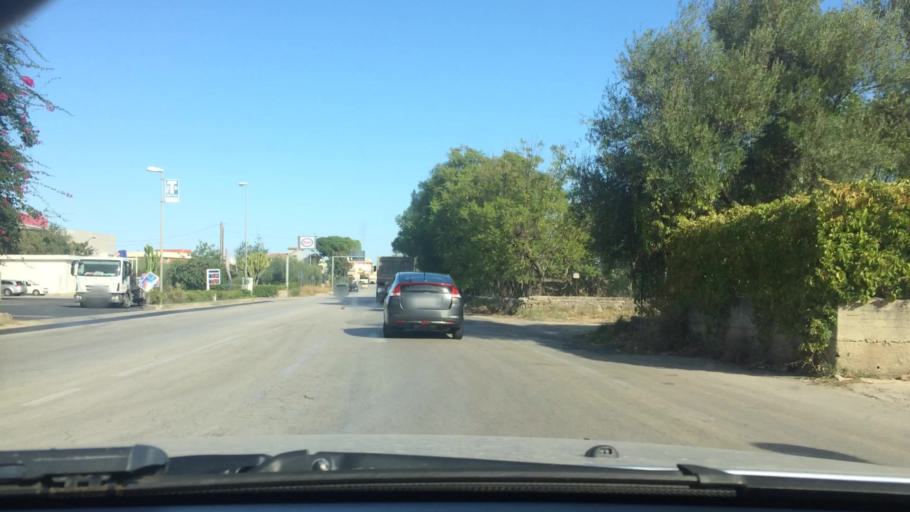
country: IT
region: Sicily
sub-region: Provincia di Siracusa
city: Priolo Gargallo
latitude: 37.1488
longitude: 15.1947
